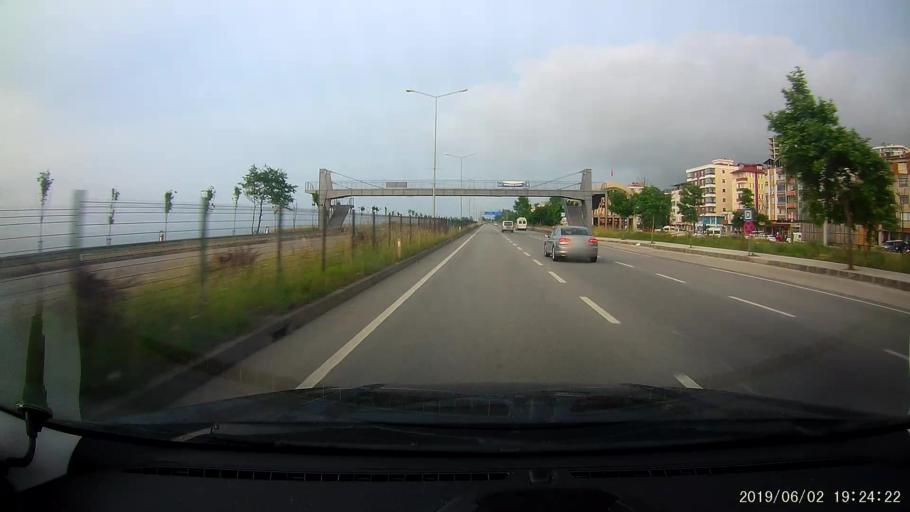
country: TR
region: Giresun
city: Bulancak
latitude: 40.9409
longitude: 38.2428
